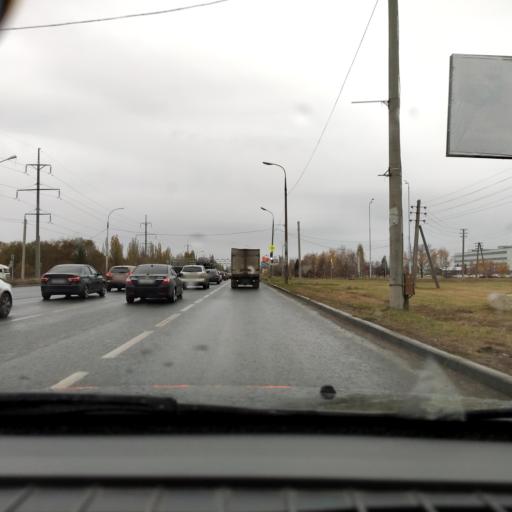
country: RU
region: Samara
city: Tol'yatti
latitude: 53.5624
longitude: 49.2908
